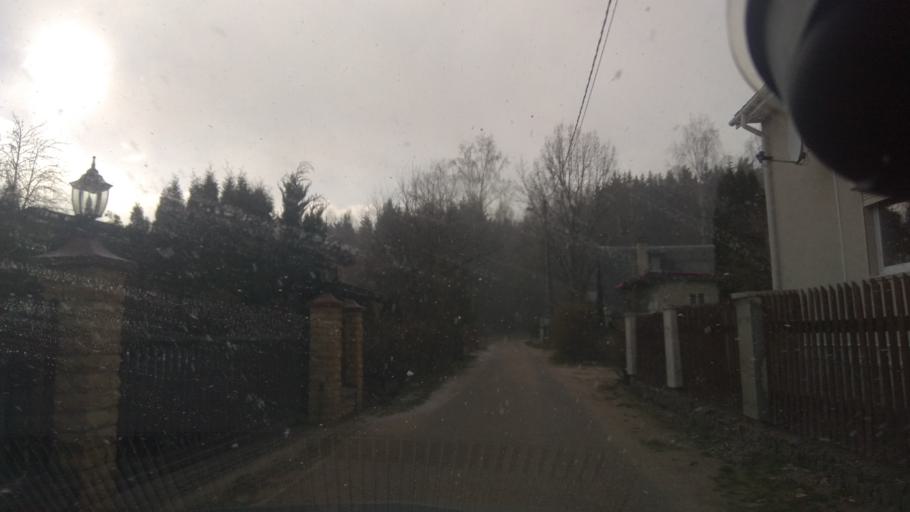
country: LT
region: Vilnius County
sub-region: Vilnius
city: Fabijoniskes
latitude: 54.7479
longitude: 25.2533
